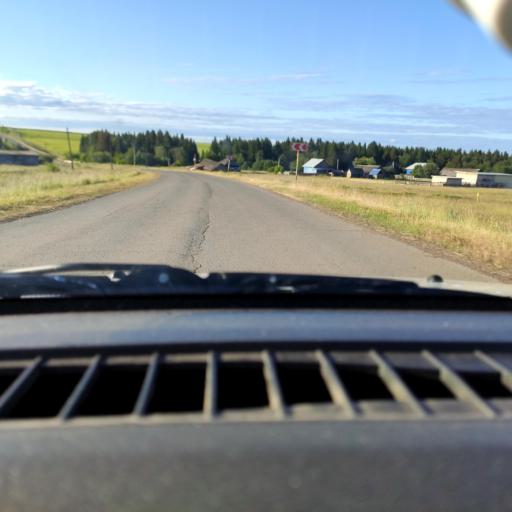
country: RU
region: Perm
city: Uinskoye
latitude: 57.0747
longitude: 56.5590
